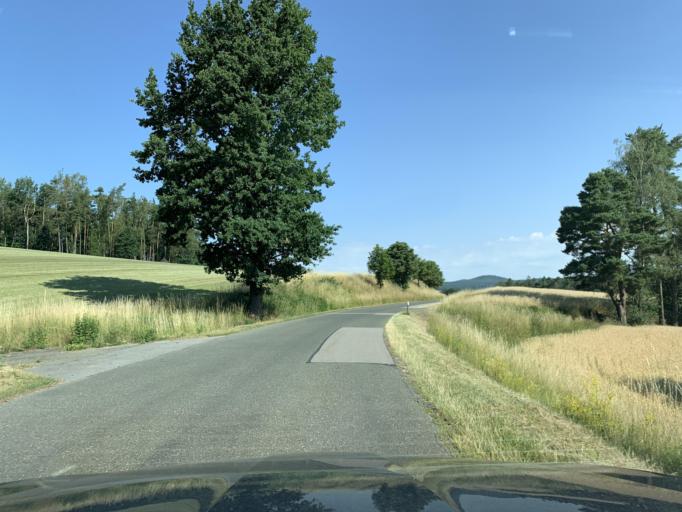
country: DE
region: Bavaria
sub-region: Upper Palatinate
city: Schwarzhofen
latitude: 49.3884
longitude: 12.3152
